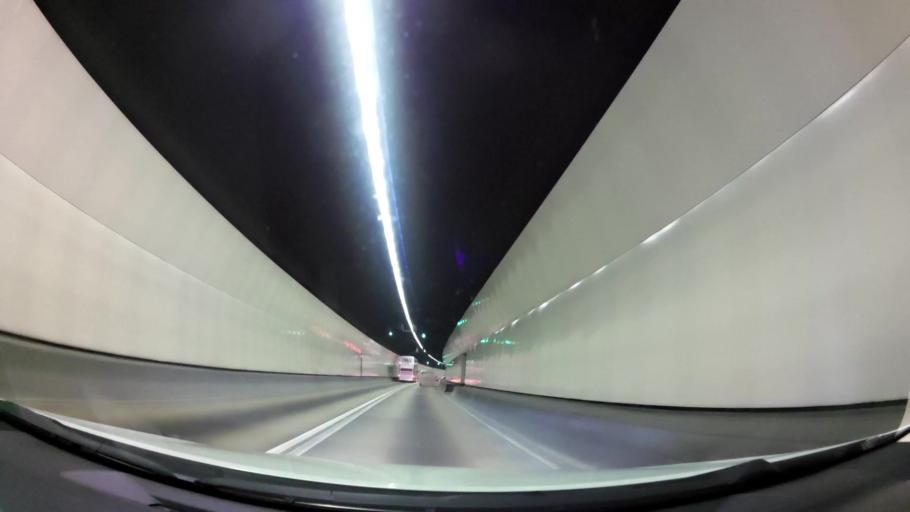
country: HK
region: Sha Tin
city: Sha Tin
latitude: 22.3769
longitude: 114.1465
